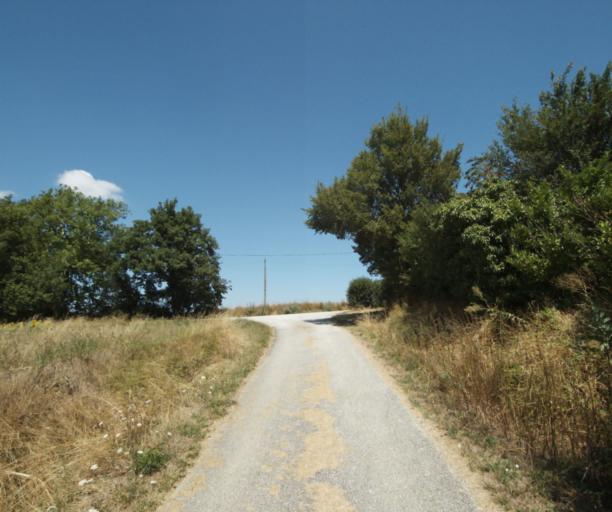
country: FR
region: Midi-Pyrenees
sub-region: Departement de la Haute-Garonne
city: Saint-Felix-Lauragais
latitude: 43.4753
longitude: 1.8644
